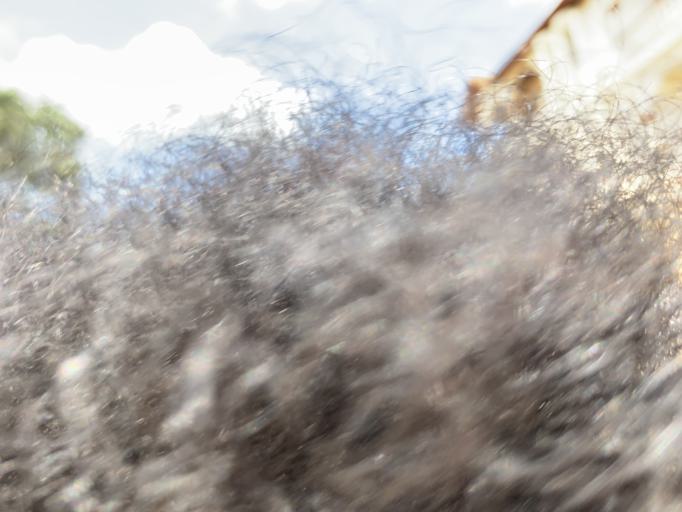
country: SL
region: Western Area
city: Waterloo
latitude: 8.3269
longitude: -13.0502
